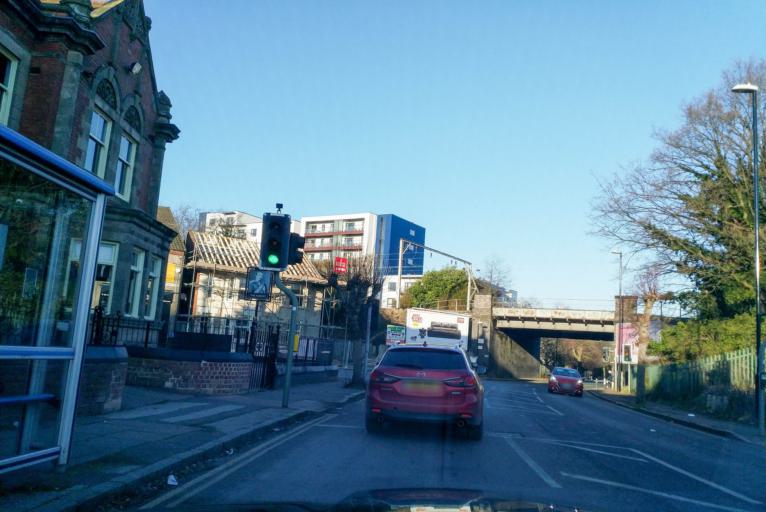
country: GB
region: England
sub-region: Coventry
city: Coventry
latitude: 52.4034
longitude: -1.5262
